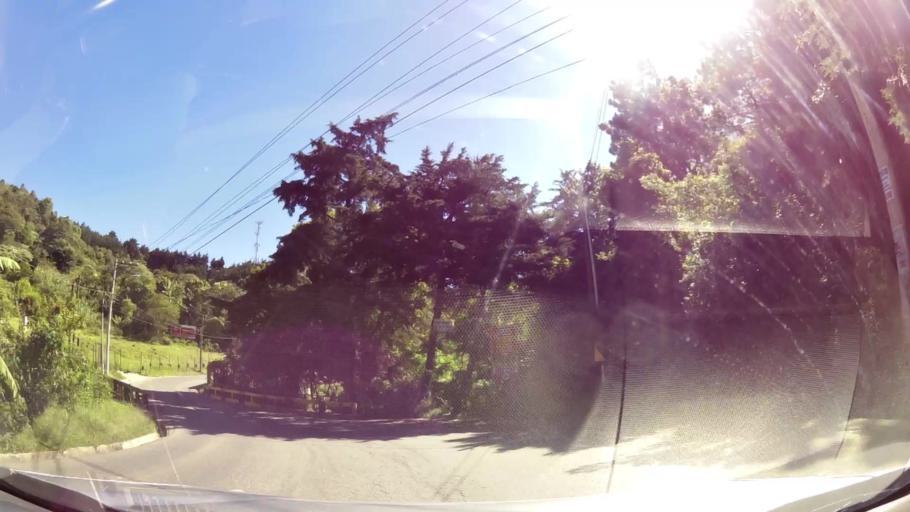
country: GT
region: Guatemala
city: San Jose Pinula
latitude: 14.5187
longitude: -90.4357
